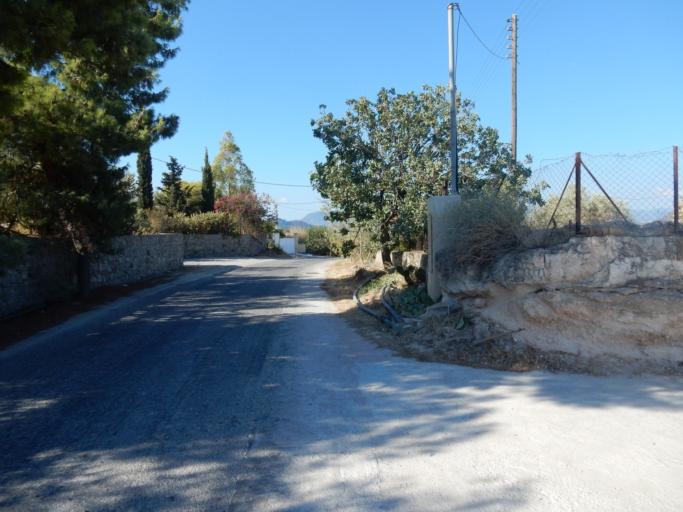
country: GR
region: Attica
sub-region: Nomos Piraios
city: Kypseli
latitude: 37.7407
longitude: 23.4508
